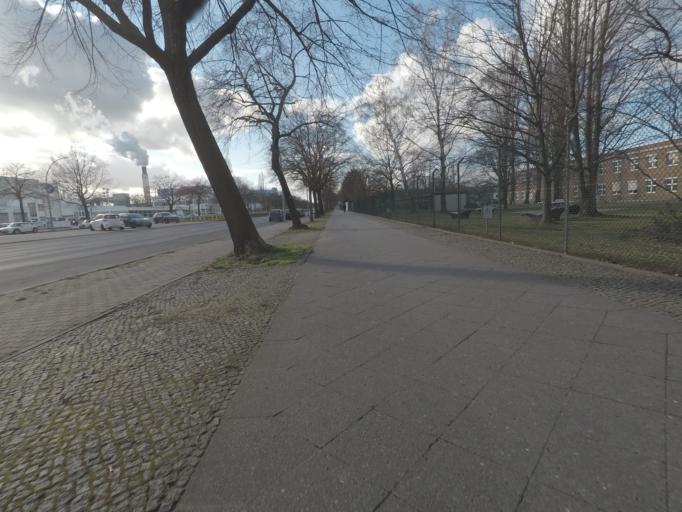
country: DE
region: Berlin
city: Siemensstadt
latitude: 52.5375
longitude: 13.2577
